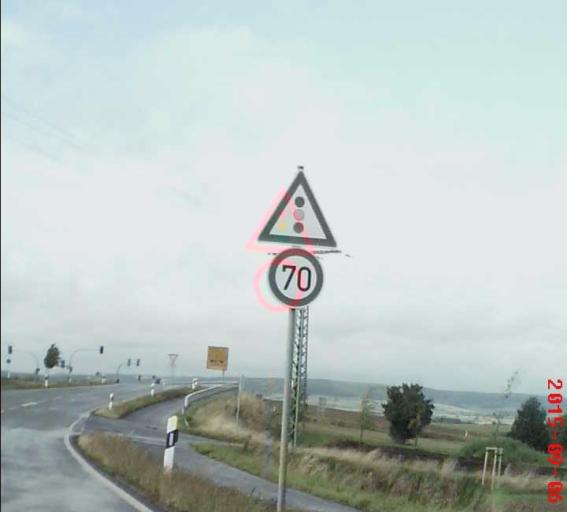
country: DE
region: Thuringia
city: Niederorschel
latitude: 51.3500
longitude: 10.4387
